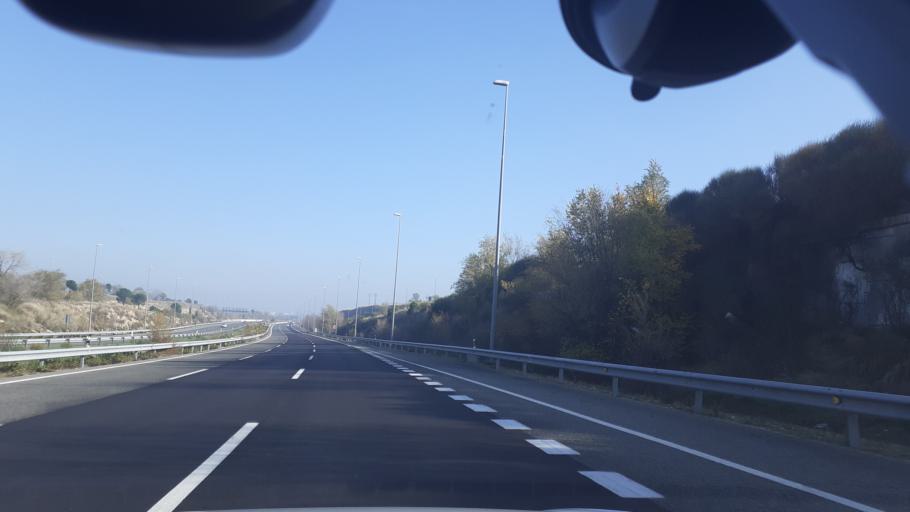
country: ES
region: Madrid
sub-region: Provincia de Madrid
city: Vicalvaro
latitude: 40.4126
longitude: -3.6083
